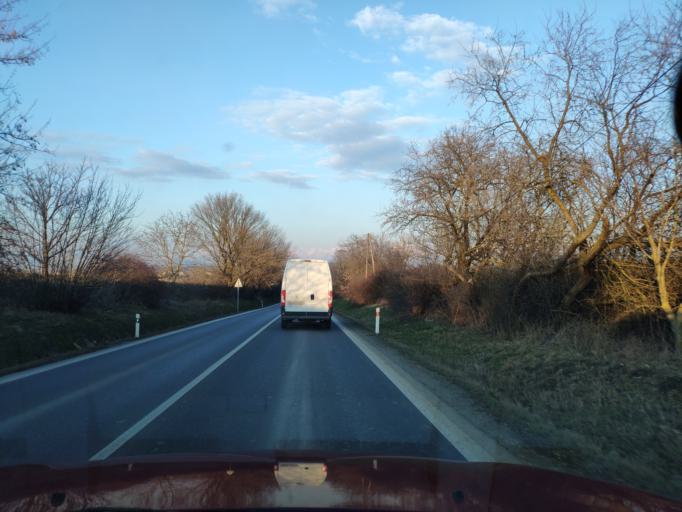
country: SK
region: Nitriansky
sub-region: Okres Nitra
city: Nitra
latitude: 48.2371
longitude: 18.0093
